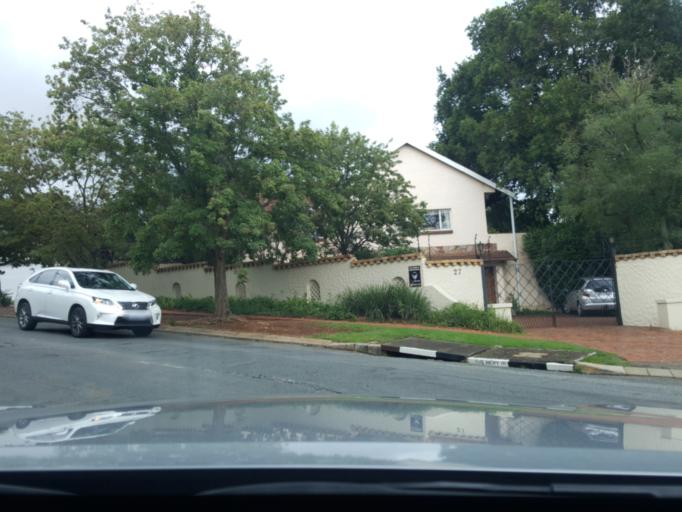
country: ZA
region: Gauteng
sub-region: City of Johannesburg Metropolitan Municipality
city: Johannesburg
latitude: -26.1284
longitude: 28.0024
